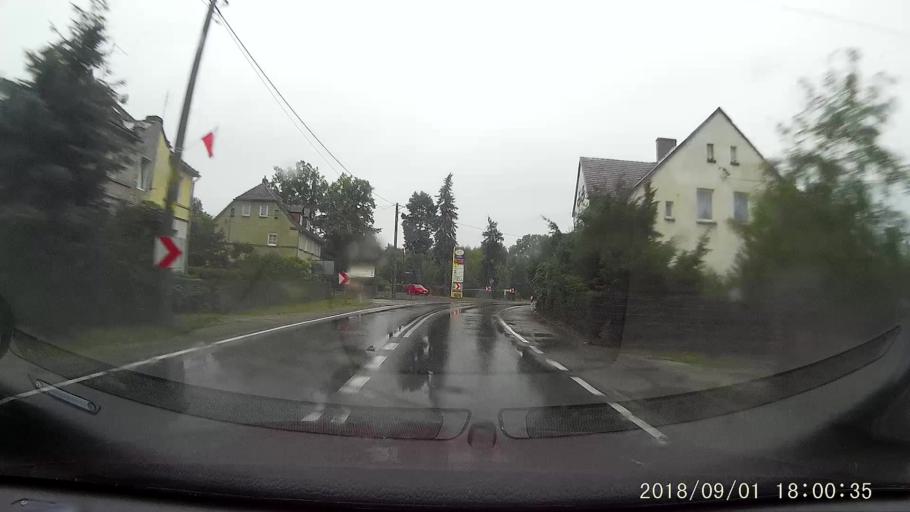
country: PL
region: Lubusz
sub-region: Powiat zaganski
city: Gozdnica
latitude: 51.4013
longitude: 15.1829
